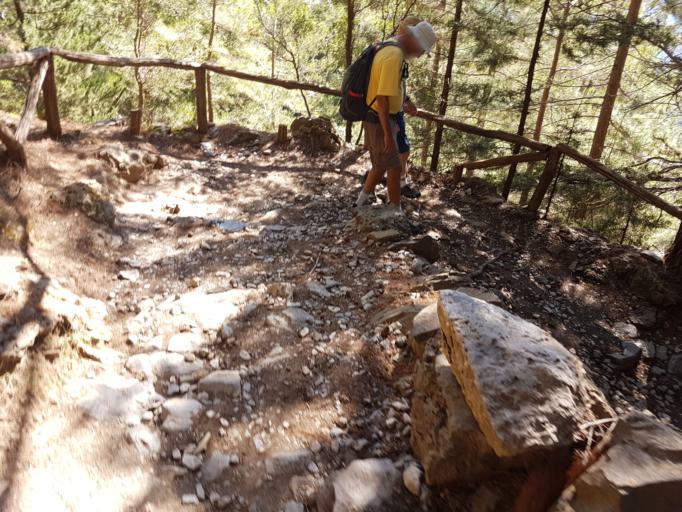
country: GR
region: Crete
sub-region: Nomos Chanias
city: Perivolia
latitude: 35.3074
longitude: 23.9249
